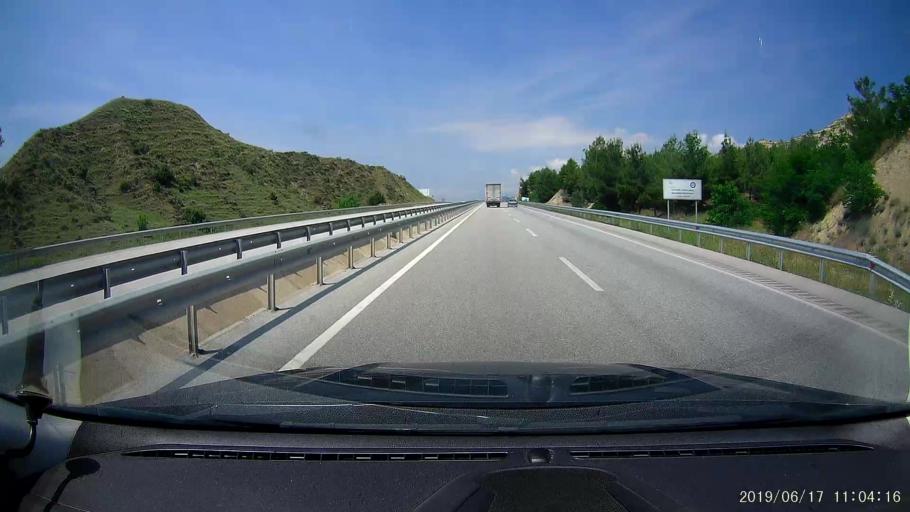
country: TR
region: Kastamonu
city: Tosya
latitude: 41.0205
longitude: 34.0981
